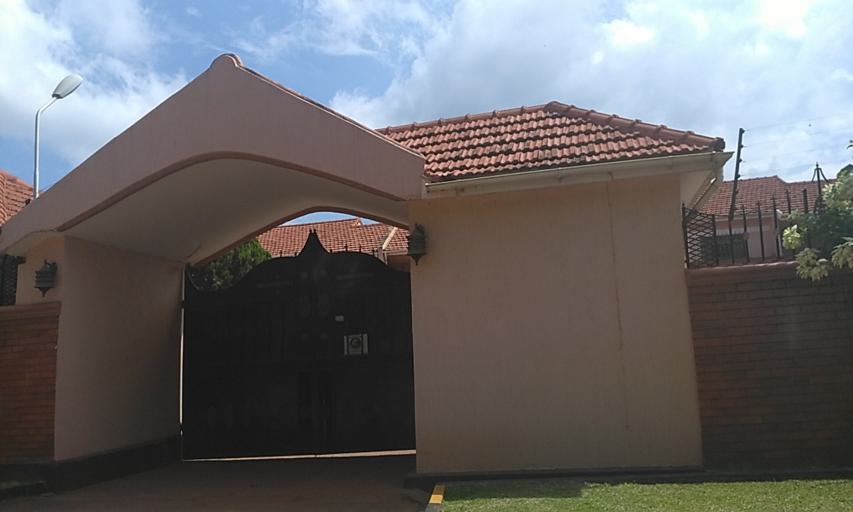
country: UG
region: Central Region
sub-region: Wakiso District
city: Kireka
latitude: 0.3455
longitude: 32.6135
